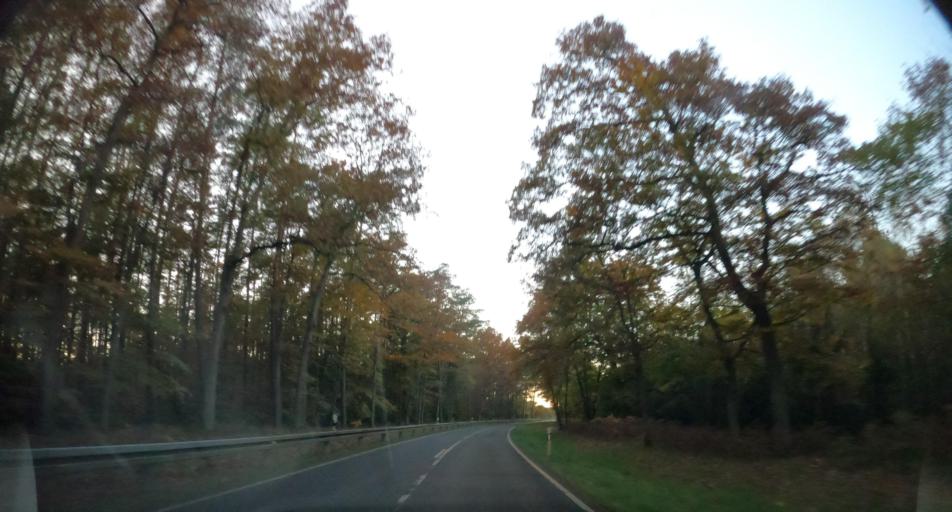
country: DE
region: Mecklenburg-Vorpommern
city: Usedom
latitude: 53.7679
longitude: 13.9227
